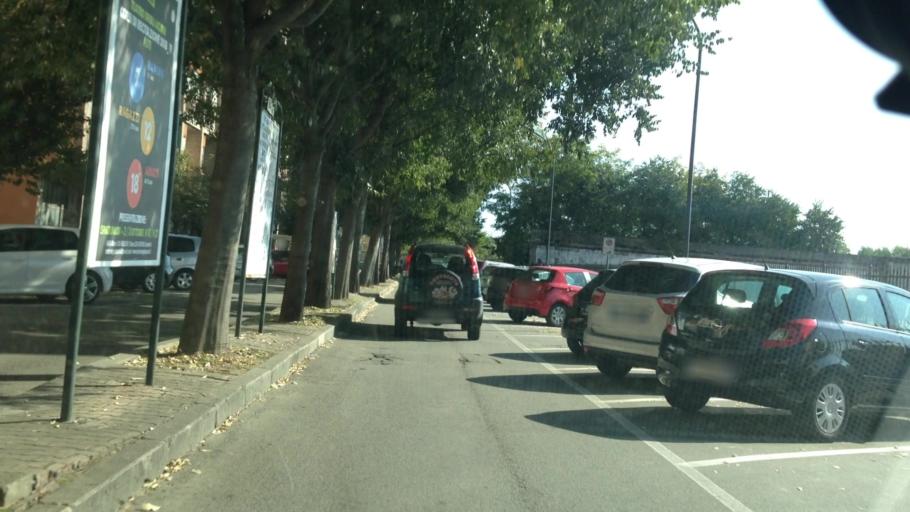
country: IT
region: Piedmont
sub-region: Provincia di Asti
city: Asti
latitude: 44.8975
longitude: 8.2153
